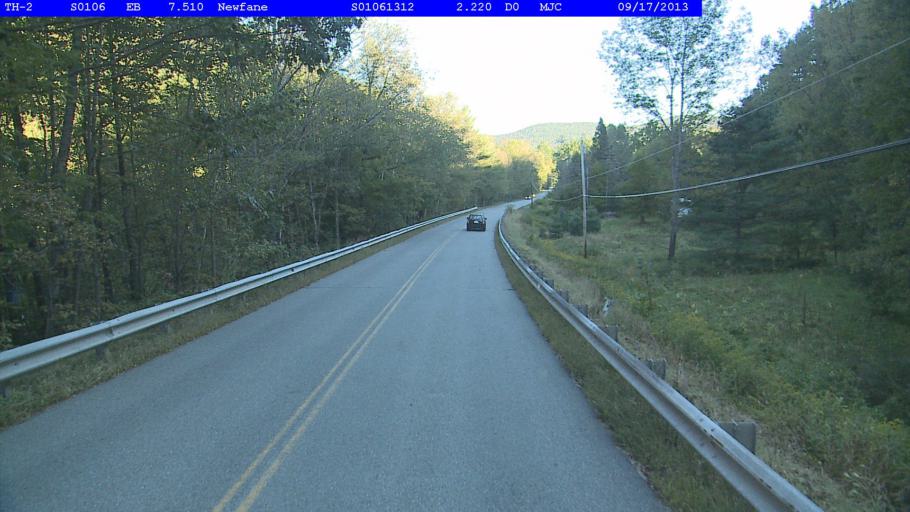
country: US
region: Vermont
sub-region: Windham County
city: Dover
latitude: 42.9444
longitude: -72.7275
